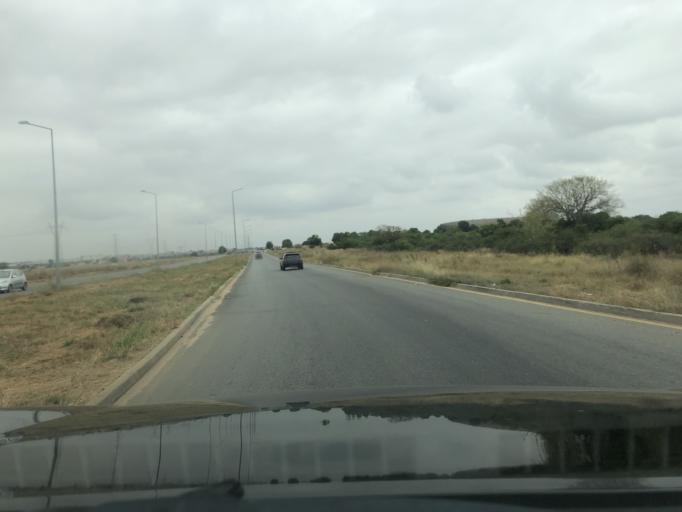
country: AO
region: Luanda
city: Luanda
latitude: -8.9759
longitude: 13.2775
